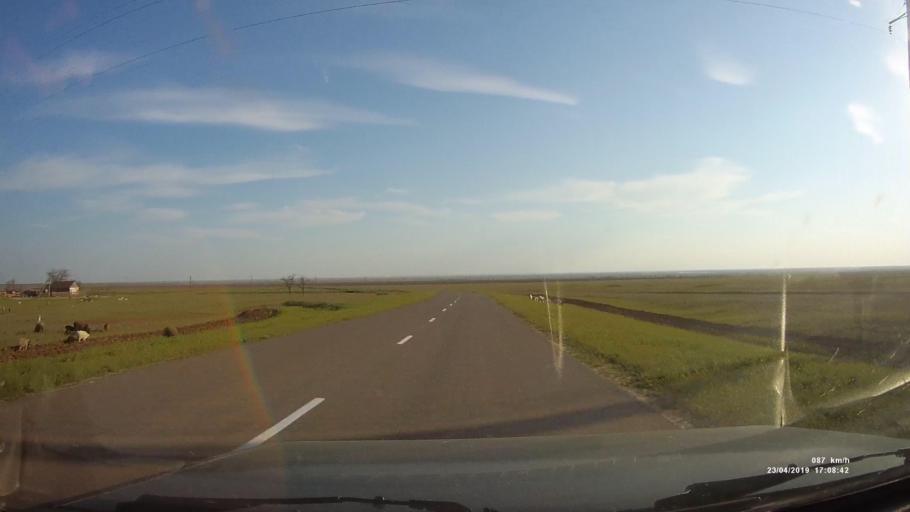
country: RU
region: Kalmykiya
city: Priyutnoye
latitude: 46.2679
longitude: 43.4855
